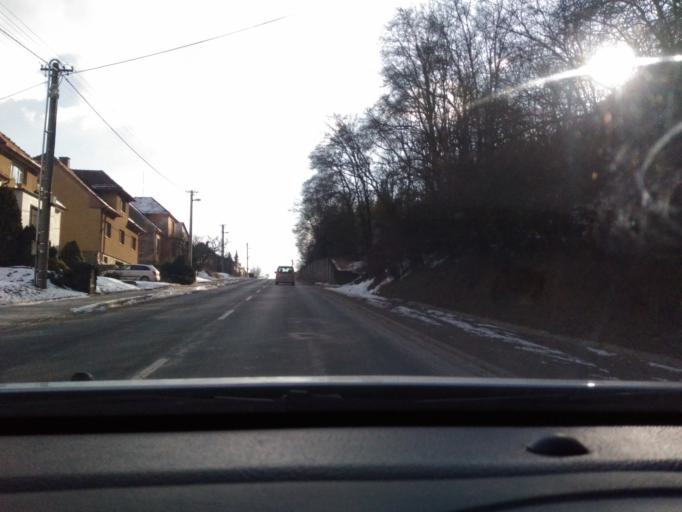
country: CZ
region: South Moravian
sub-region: Okres Brno-Venkov
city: Nedvedice
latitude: 49.4204
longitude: 16.3524
